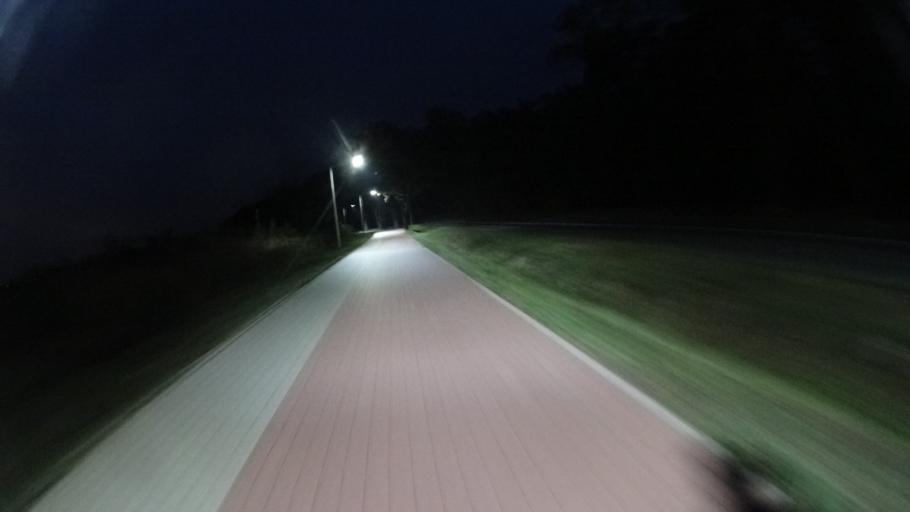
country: PL
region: Masovian Voivodeship
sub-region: Powiat warszawski zachodni
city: Ozarow Mazowiecki
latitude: 52.2318
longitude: 20.8130
